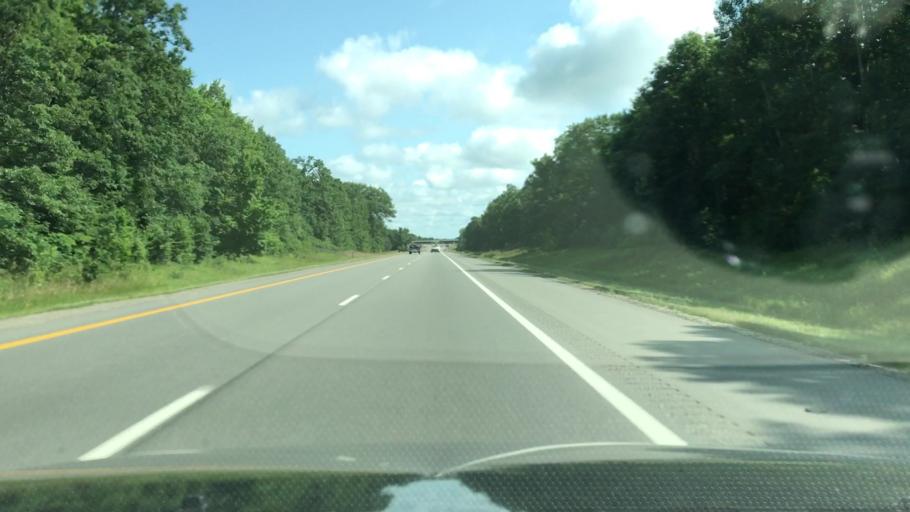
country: US
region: Michigan
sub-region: Montcalm County
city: Howard City
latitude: 43.4497
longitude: -85.4856
